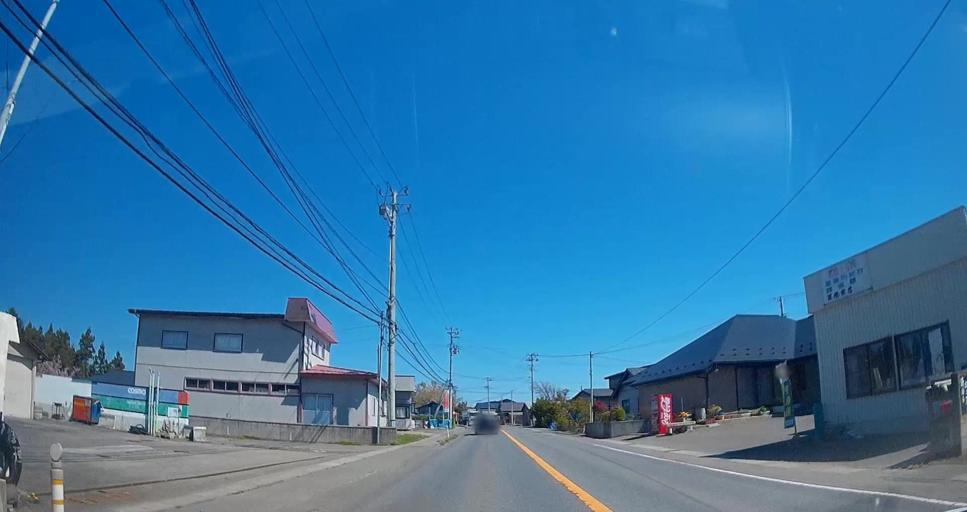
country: JP
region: Aomori
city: Misawa
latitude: 40.7874
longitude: 141.3998
